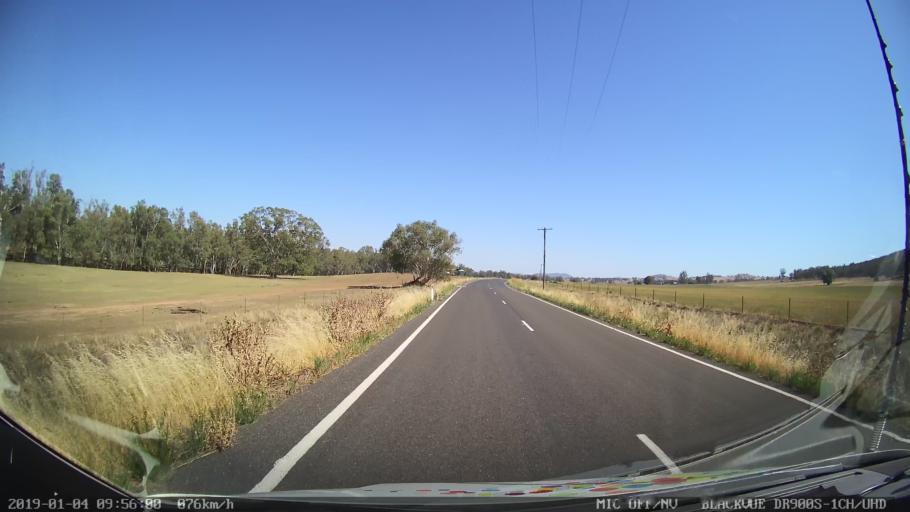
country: AU
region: New South Wales
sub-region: Cabonne
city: Canowindra
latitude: -33.5292
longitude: 148.4006
